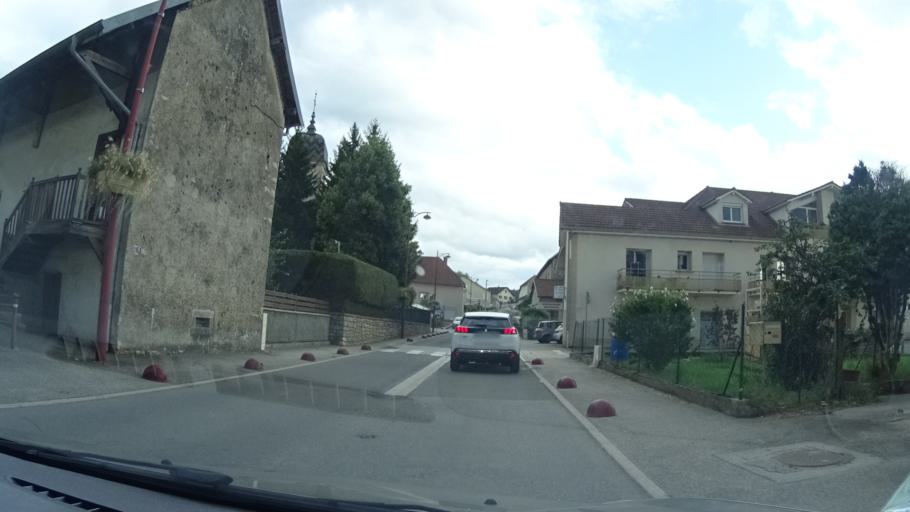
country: FR
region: Franche-Comte
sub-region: Departement du Doubs
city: Saone
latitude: 47.2259
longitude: 6.1166
